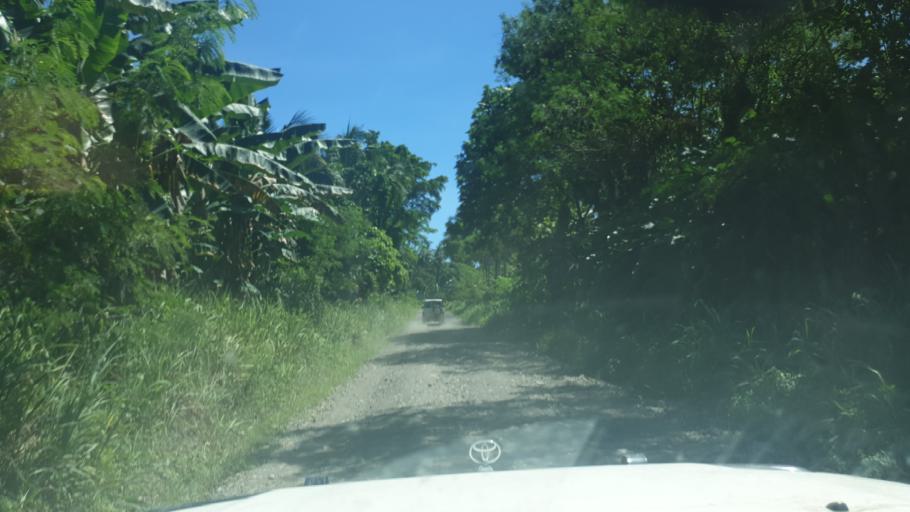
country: PG
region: Bougainville
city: Buka
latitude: -5.6699
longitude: 155.1035
